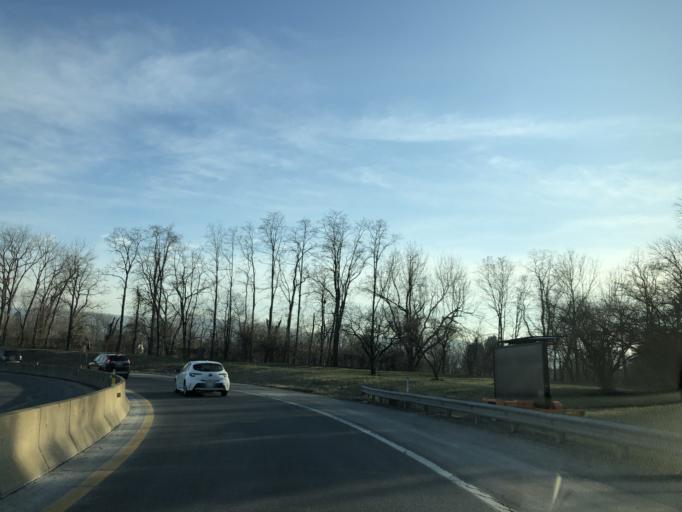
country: US
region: Pennsylvania
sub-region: Chester County
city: Elverson
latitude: 40.1587
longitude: -75.8821
